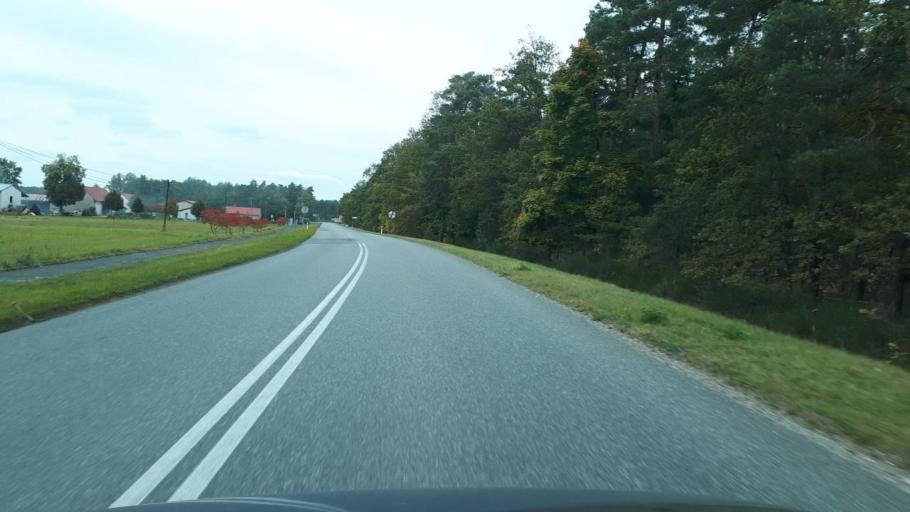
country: PL
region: Opole Voivodeship
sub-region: Powiat oleski
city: Dobrodzien
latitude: 50.7699
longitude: 18.4301
